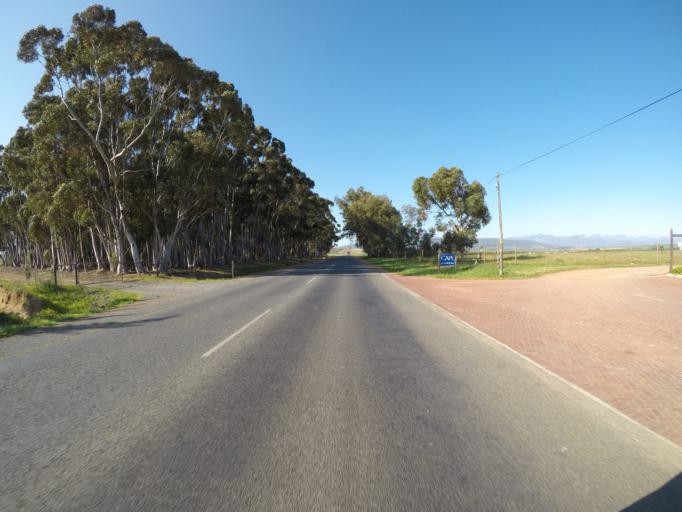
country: ZA
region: Western Cape
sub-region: City of Cape Town
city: Kraaifontein
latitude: -33.7594
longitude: 18.8097
